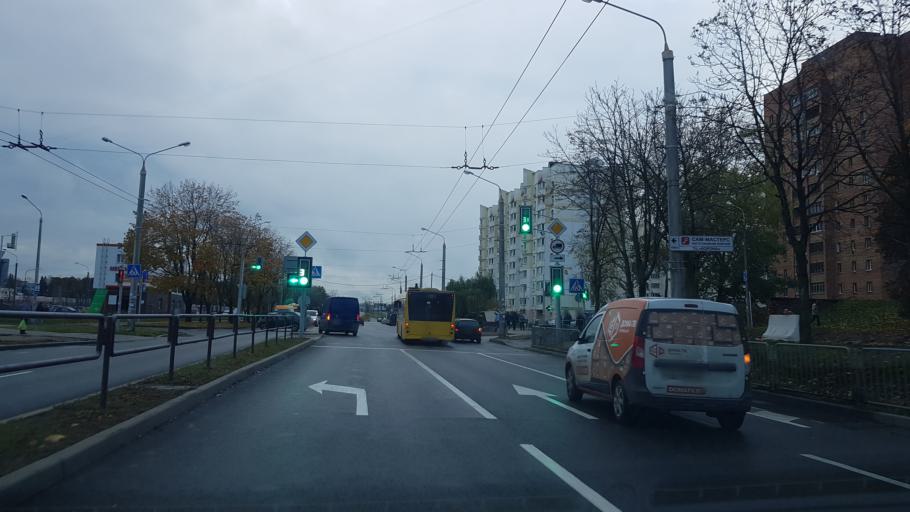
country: BY
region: Minsk
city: Syenitsa
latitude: 53.8436
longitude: 27.5294
